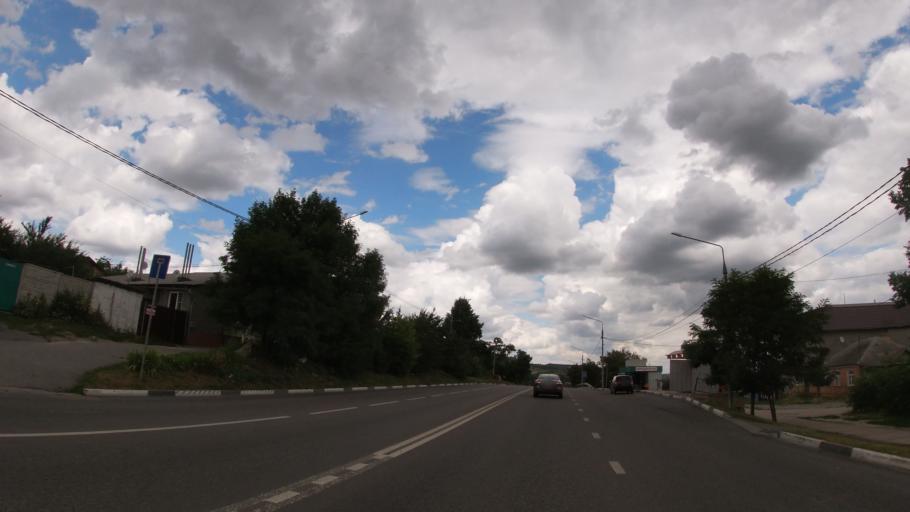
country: RU
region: Belgorod
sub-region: Belgorodskiy Rayon
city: Belgorod
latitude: 50.6032
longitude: 36.6100
